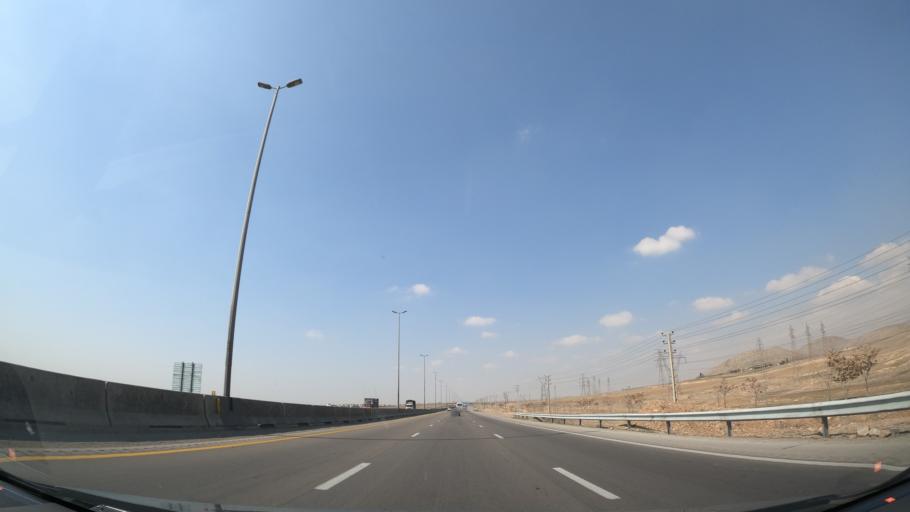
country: IR
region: Qazvin
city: Abyek
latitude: 36.0599
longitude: 50.4990
